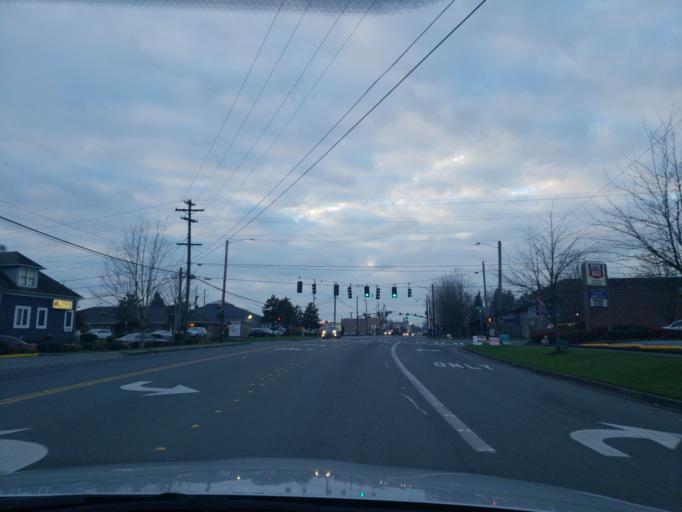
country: US
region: Washington
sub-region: Snohomish County
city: Snohomish
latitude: 47.9127
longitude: -122.0853
